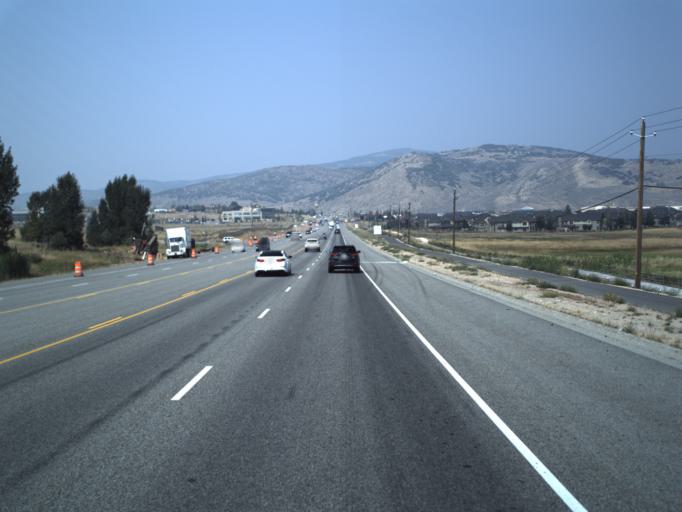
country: US
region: Utah
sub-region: Summit County
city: Snyderville
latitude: 40.7139
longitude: -111.5447
